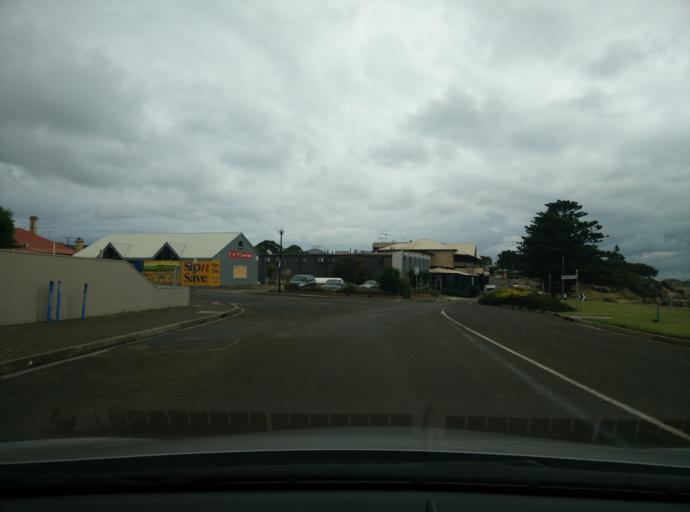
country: AU
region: South Australia
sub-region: Kangaroo Island
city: Kingscote
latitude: -35.6566
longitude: 137.6396
